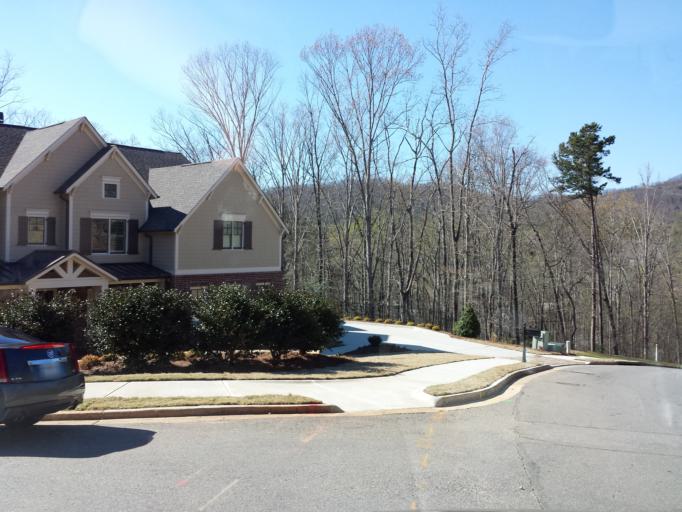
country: US
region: Georgia
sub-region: Cobb County
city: Marietta
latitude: 33.9597
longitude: -84.5752
